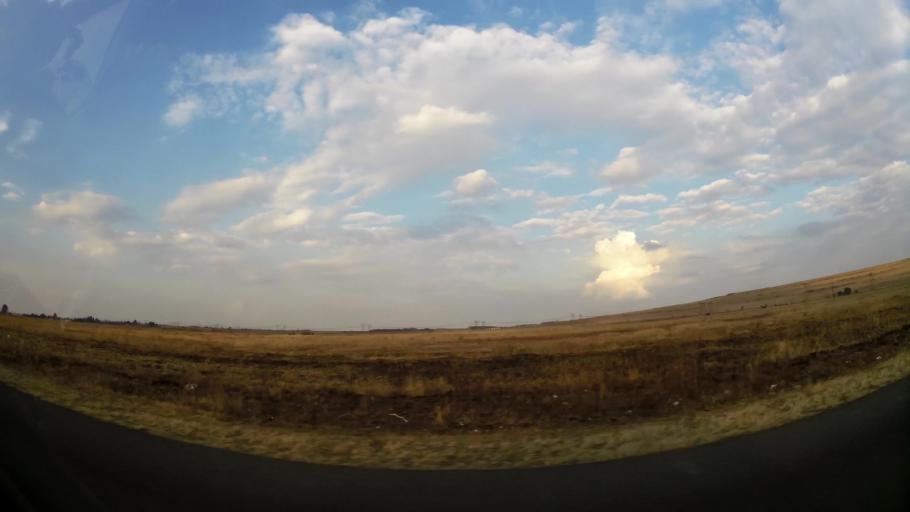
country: ZA
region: Gauteng
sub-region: Sedibeng District Municipality
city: Vanderbijlpark
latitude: -26.6273
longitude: 27.8100
